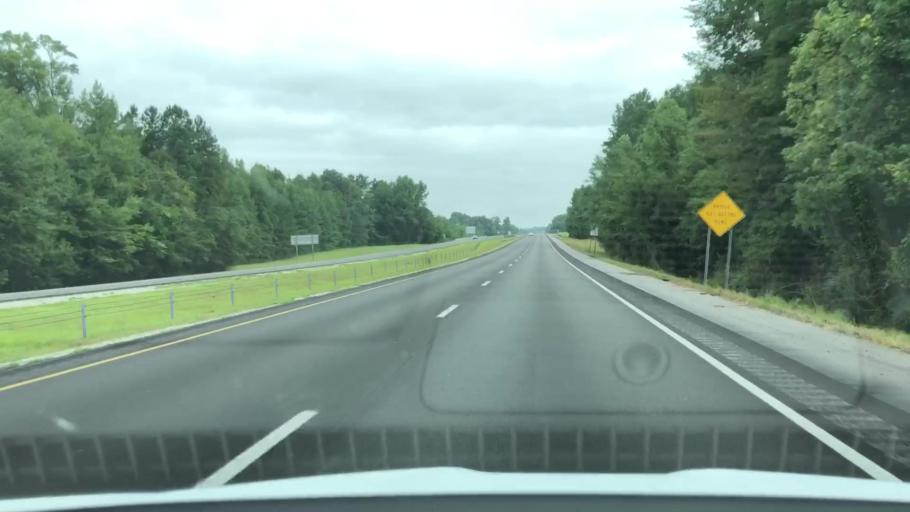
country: US
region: North Carolina
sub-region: Wayne County
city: Fremont
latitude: 35.5585
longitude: -77.9872
